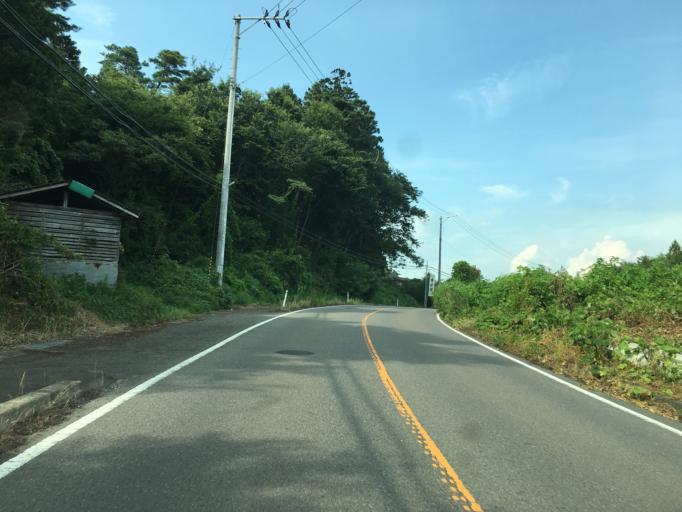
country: JP
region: Fukushima
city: Koriyama
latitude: 37.3576
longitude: 140.4171
